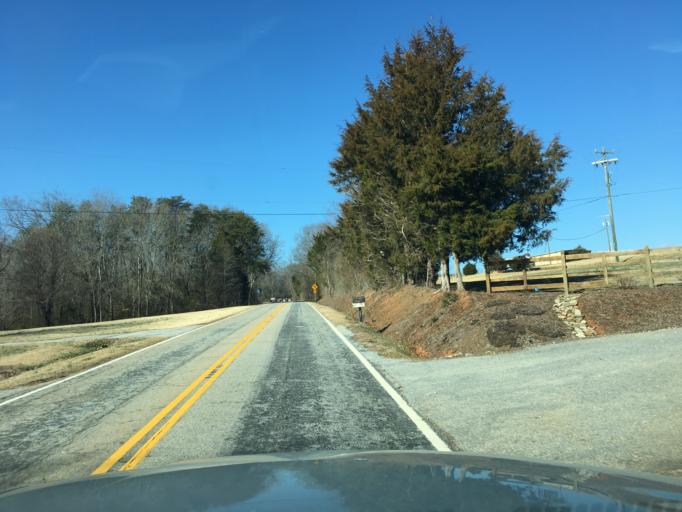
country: US
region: South Carolina
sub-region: Pickens County
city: Pickens
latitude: 34.8585
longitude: -82.7477
